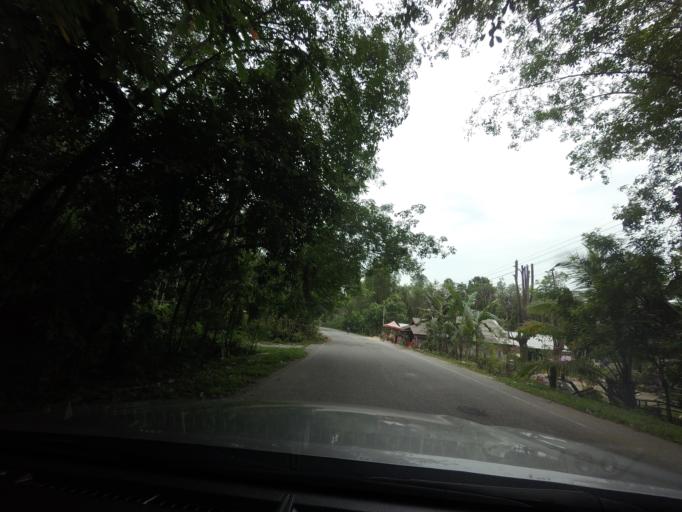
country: TH
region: Narathiwat
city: Rueso
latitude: 6.3506
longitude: 101.4752
